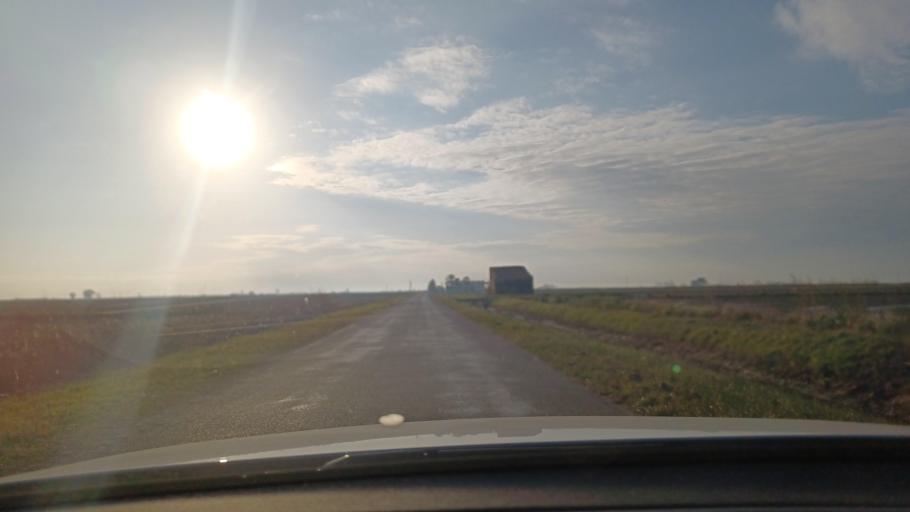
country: ES
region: Catalonia
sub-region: Provincia de Tarragona
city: Deltebre
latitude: 40.6866
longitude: 0.6531
